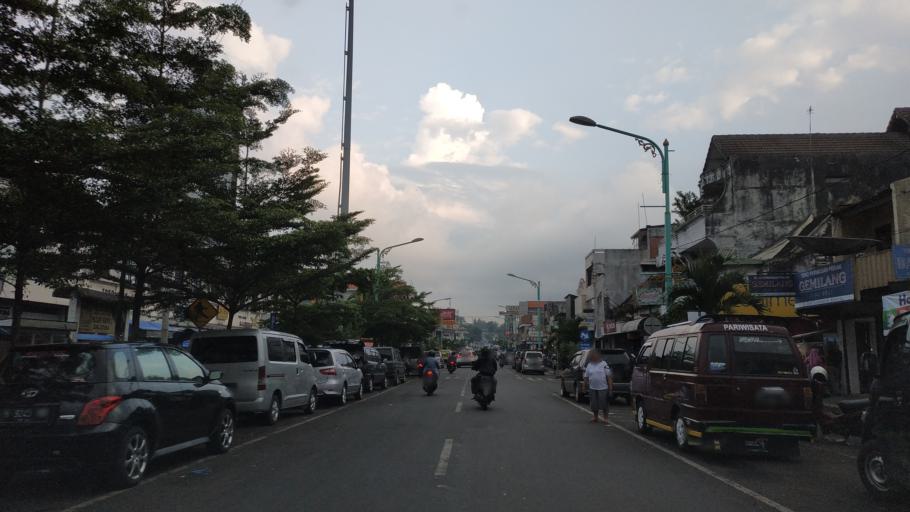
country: ID
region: Central Java
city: Salatiga
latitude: -7.3300
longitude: 110.5047
